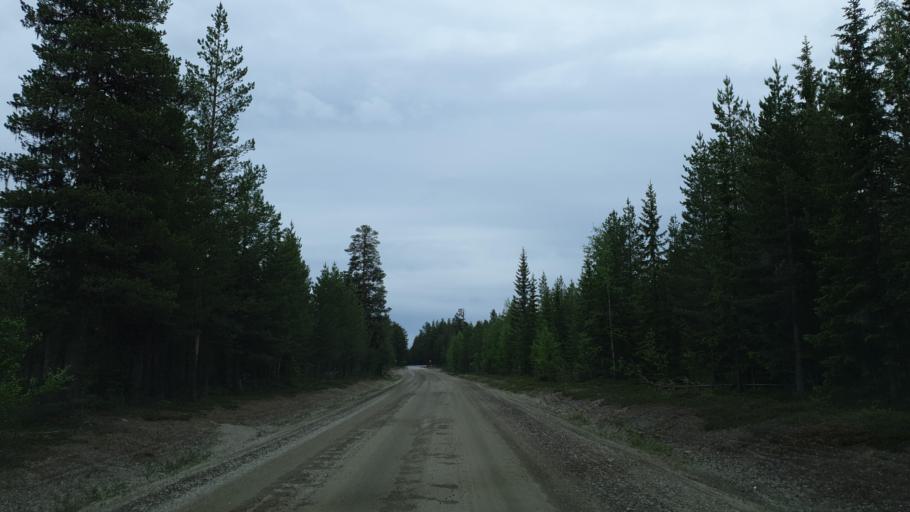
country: SE
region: Vaesterbotten
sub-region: Sorsele Kommun
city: Sorsele
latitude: 65.5540
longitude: 17.5065
